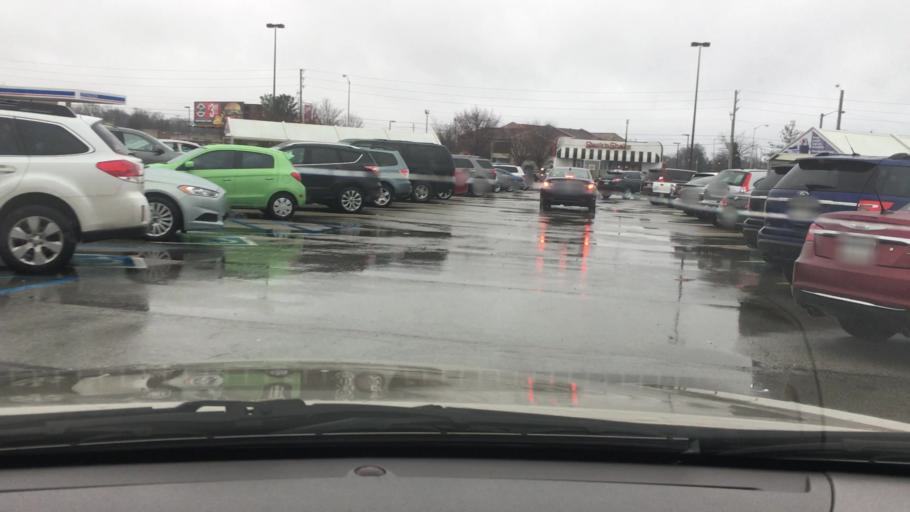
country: US
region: Indiana
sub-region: Marion County
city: Lawrence
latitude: 39.8844
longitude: -86.0692
